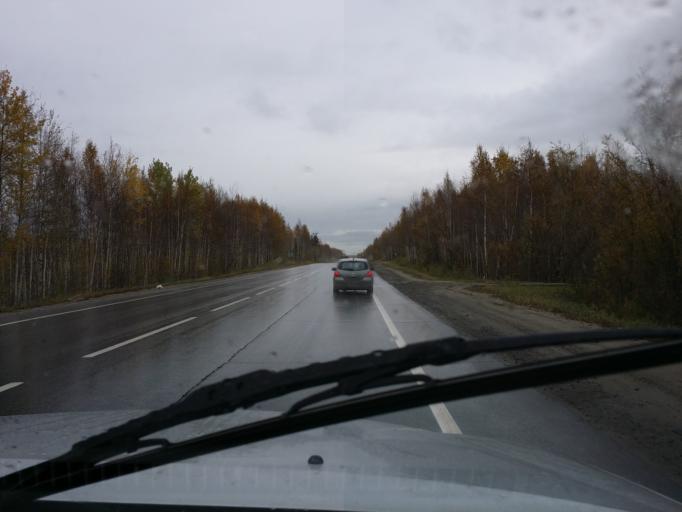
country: RU
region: Khanty-Mansiyskiy Avtonomnyy Okrug
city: Megion
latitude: 61.0639
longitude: 76.1153
